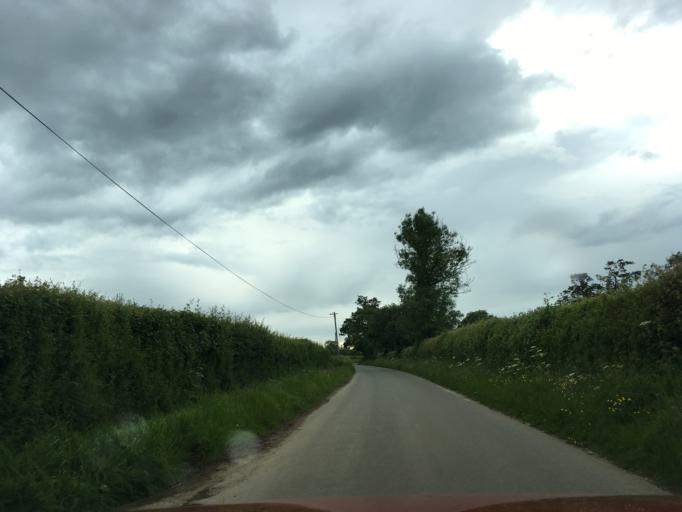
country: GB
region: England
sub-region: Wiltshire
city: Luckington
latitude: 51.5731
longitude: -2.2352
